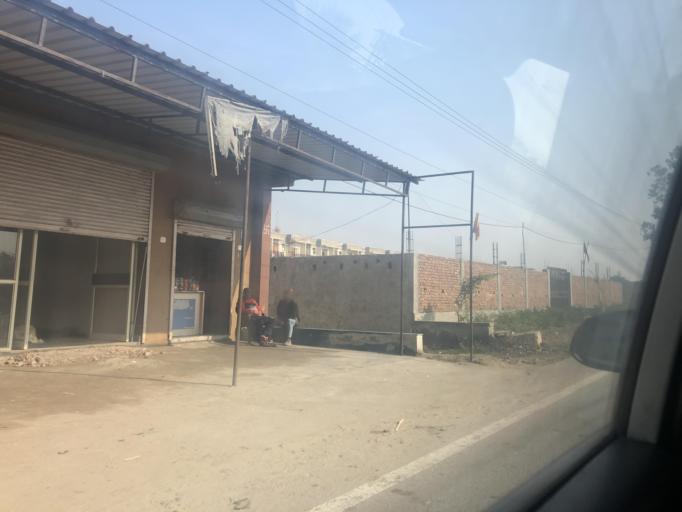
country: IN
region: Haryana
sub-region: Jhajjar
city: Bahadurgarh
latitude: 28.6868
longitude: 76.8935
